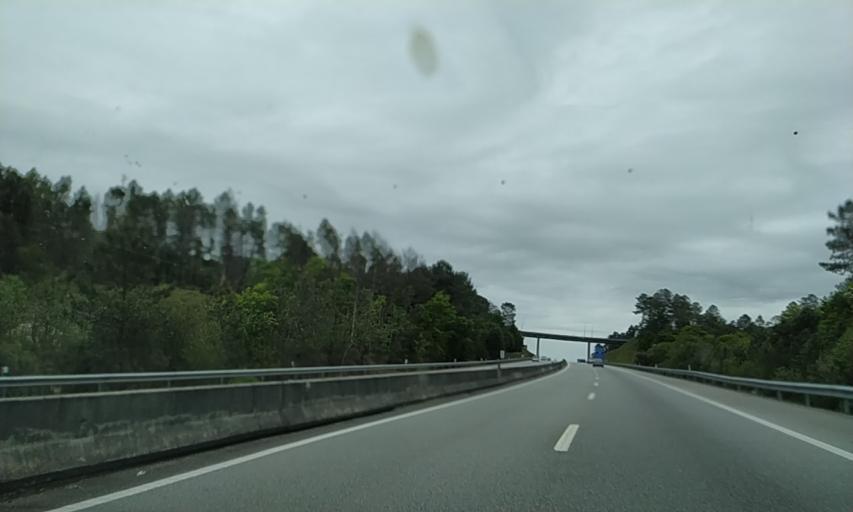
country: PT
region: Viseu
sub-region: Viseu
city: Viseu
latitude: 40.6240
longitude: -7.9494
